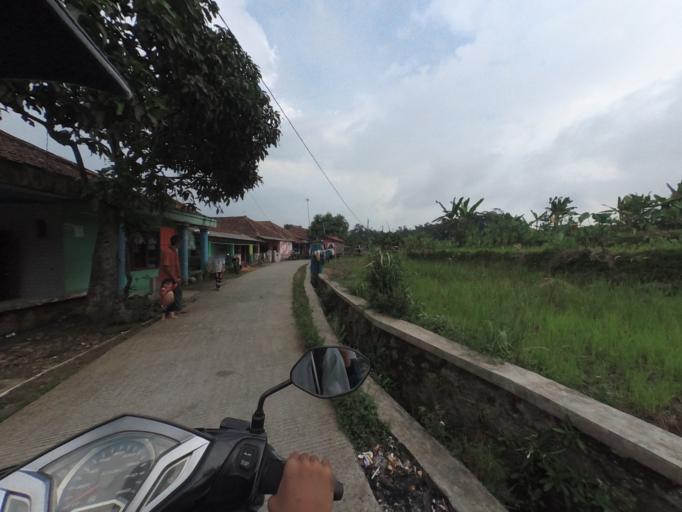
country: ID
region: West Java
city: Ciampea
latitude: -6.6889
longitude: 106.6530
